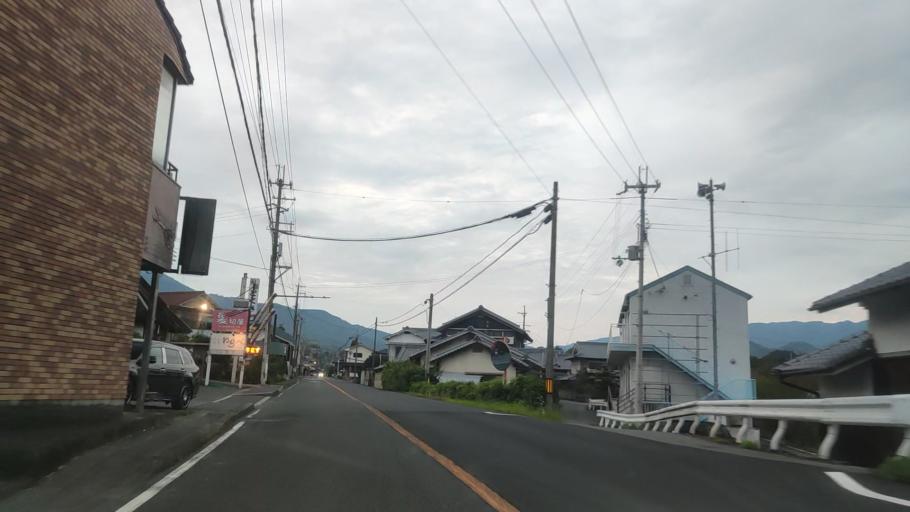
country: JP
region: Wakayama
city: Hashimoto
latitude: 34.3292
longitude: 135.6079
